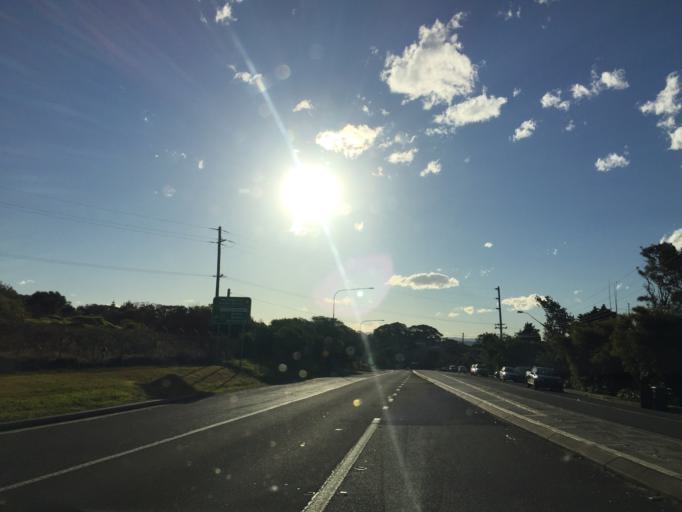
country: AU
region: New South Wales
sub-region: Kiama
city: Kiama
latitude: -34.6497
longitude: 150.8544
